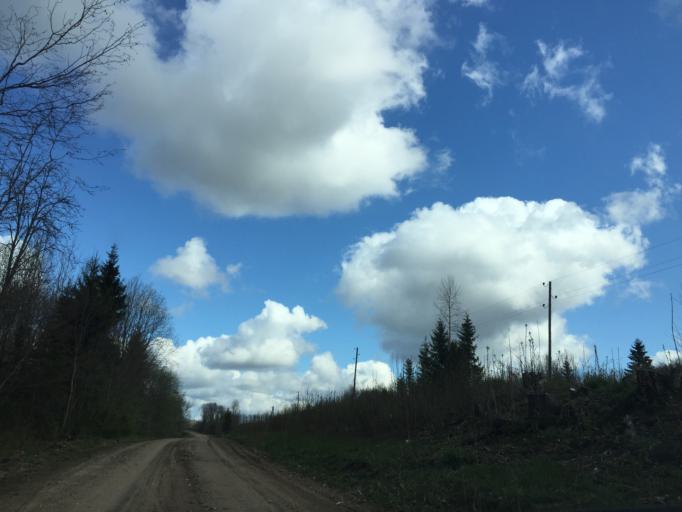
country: LV
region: Apes Novads
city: Ape
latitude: 57.5490
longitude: 26.8879
